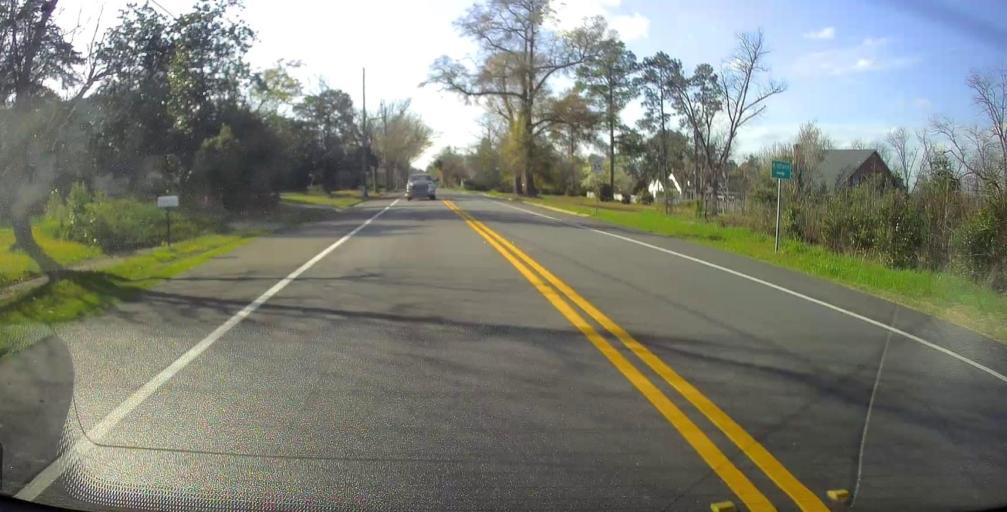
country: US
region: Georgia
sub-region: Montgomery County
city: Mount Vernon
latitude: 32.1838
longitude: -82.5653
